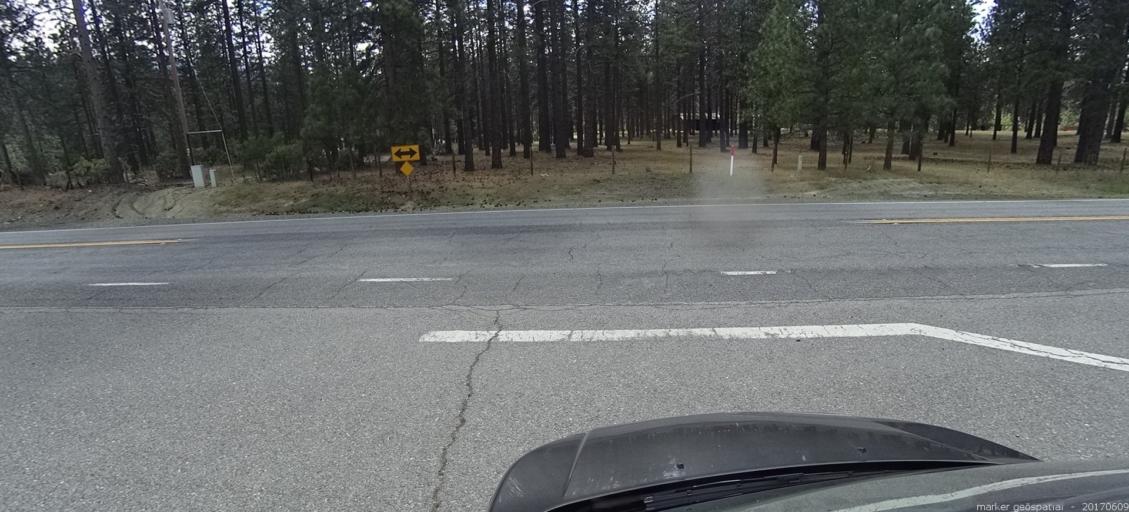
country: US
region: California
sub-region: Siskiyou County
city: Yreka
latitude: 41.5149
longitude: -122.9066
